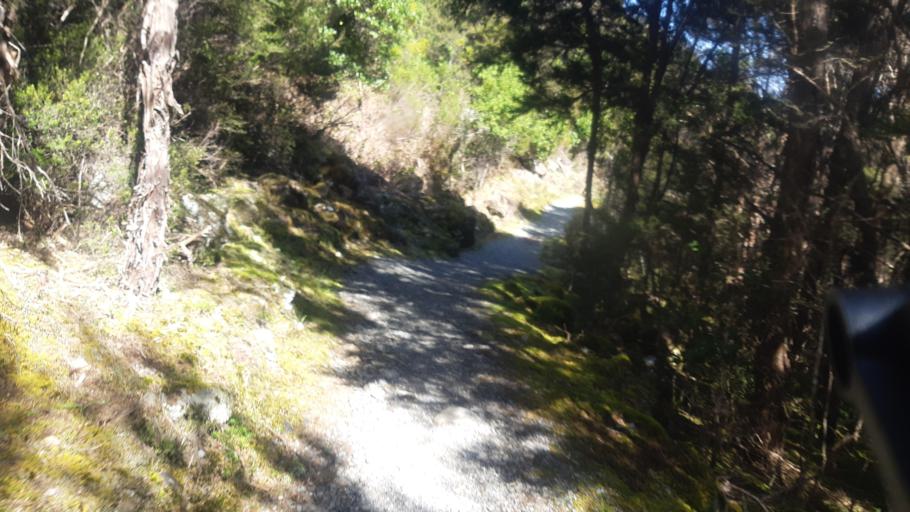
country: NZ
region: Tasman
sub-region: Tasman District
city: Wakefield
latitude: -41.7948
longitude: 172.8348
